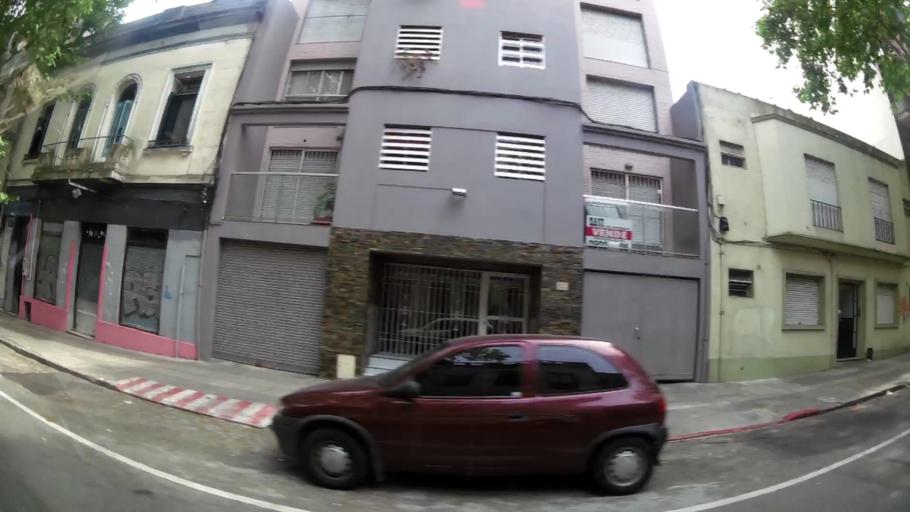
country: UY
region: Montevideo
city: Montevideo
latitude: -34.9092
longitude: -56.1985
